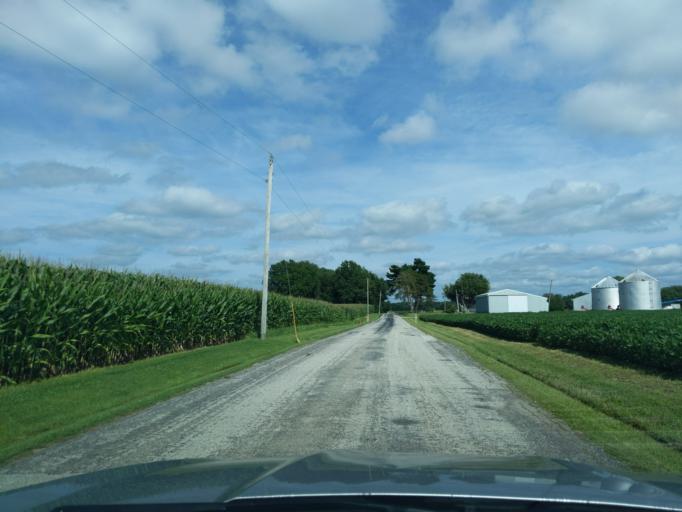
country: US
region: Indiana
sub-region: Decatur County
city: Greensburg
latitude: 39.2349
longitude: -85.3883
